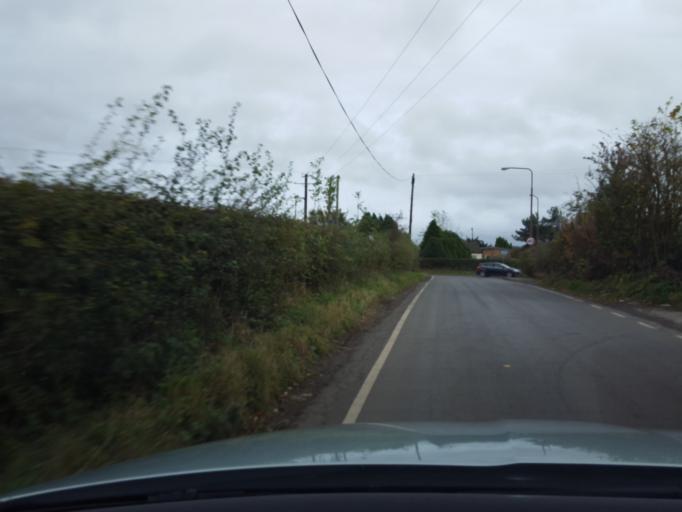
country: GB
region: Scotland
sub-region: West Lothian
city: East Calder
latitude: 55.8988
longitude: -3.4458
